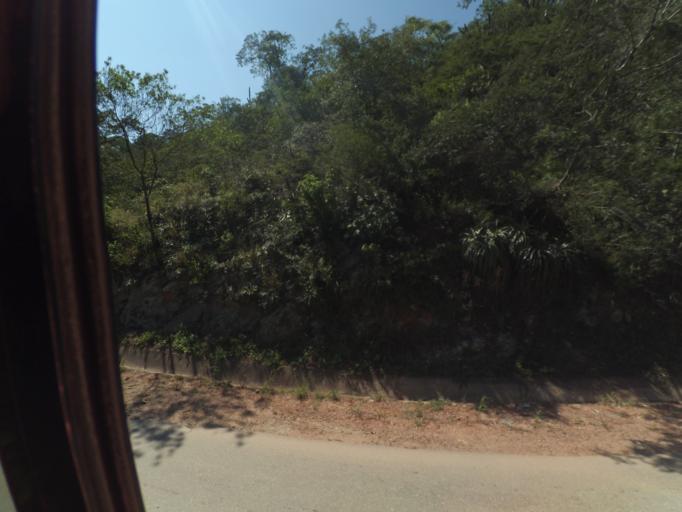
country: BO
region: Santa Cruz
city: Mairana
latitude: -18.1521
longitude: -63.9275
